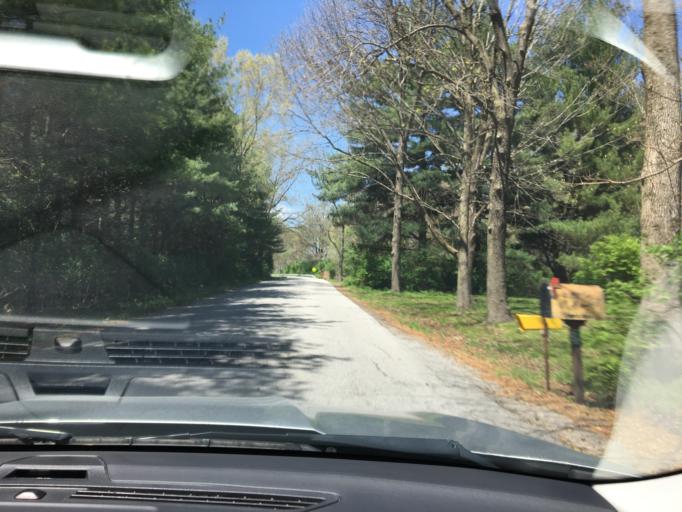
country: US
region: Indiana
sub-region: Tippecanoe County
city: Dayton
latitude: 40.3153
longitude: -86.7549
